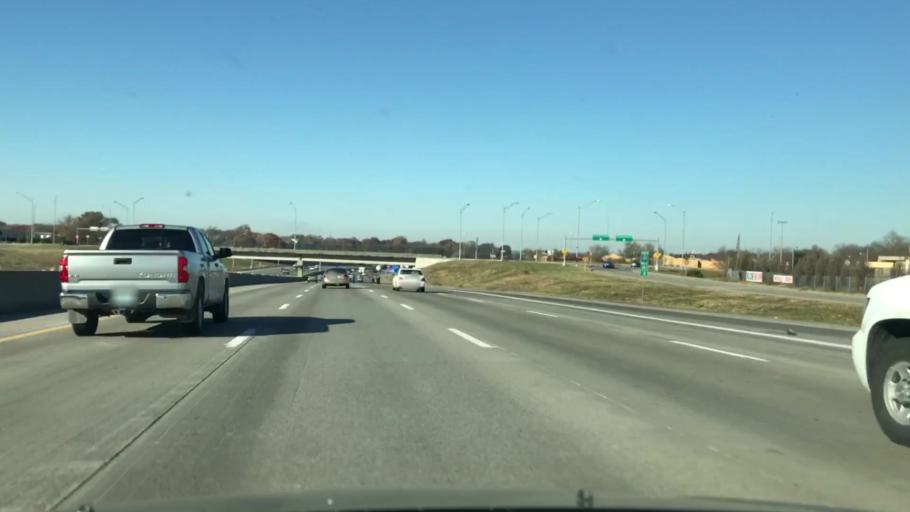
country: US
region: Missouri
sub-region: Jackson County
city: Grandview
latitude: 38.9144
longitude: -94.5256
